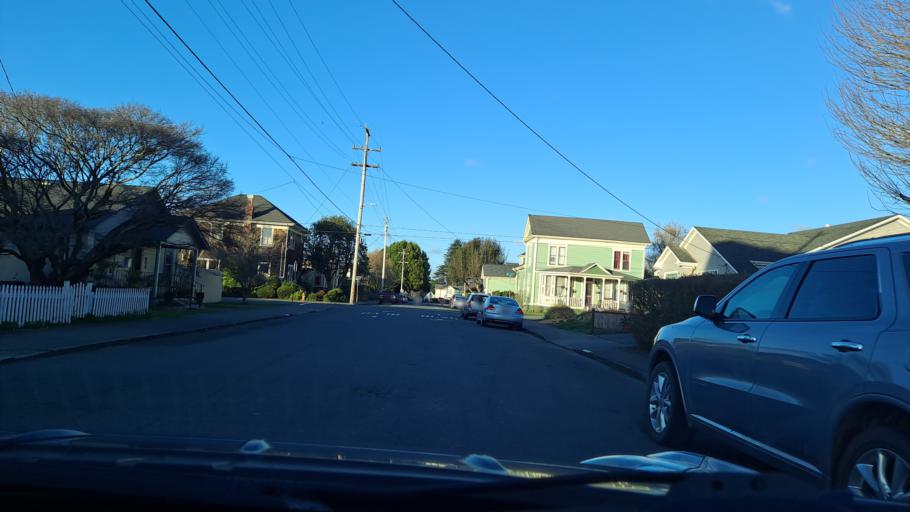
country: US
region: California
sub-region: Humboldt County
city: Arcata
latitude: 40.8736
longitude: -124.0862
